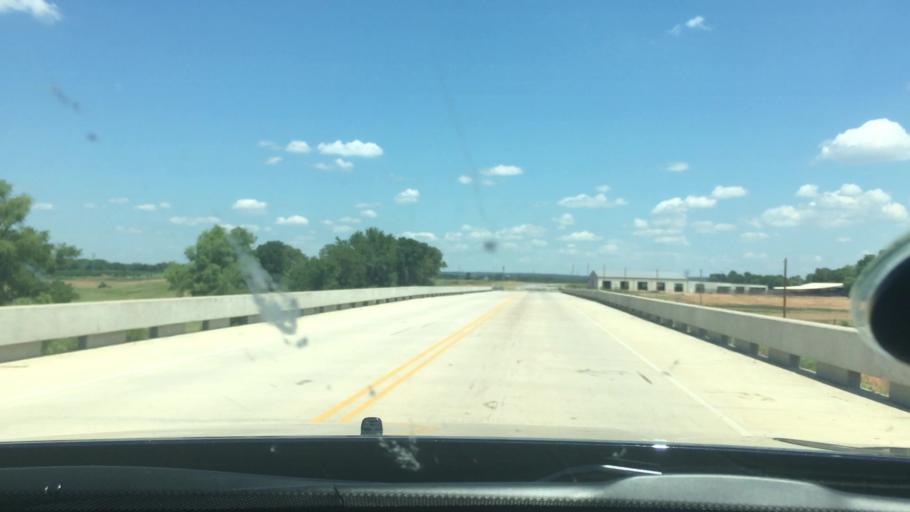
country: US
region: Oklahoma
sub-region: Carter County
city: Dickson
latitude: 34.2340
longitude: -96.9761
